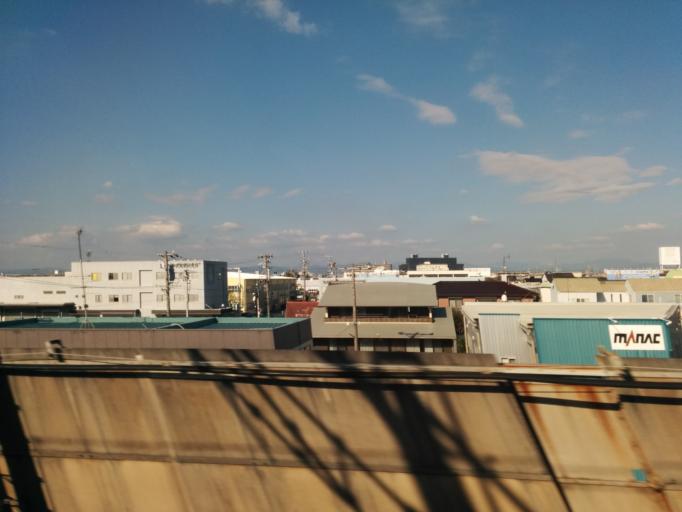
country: JP
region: Shizuoka
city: Hamamatsu
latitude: 34.7088
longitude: 137.7788
